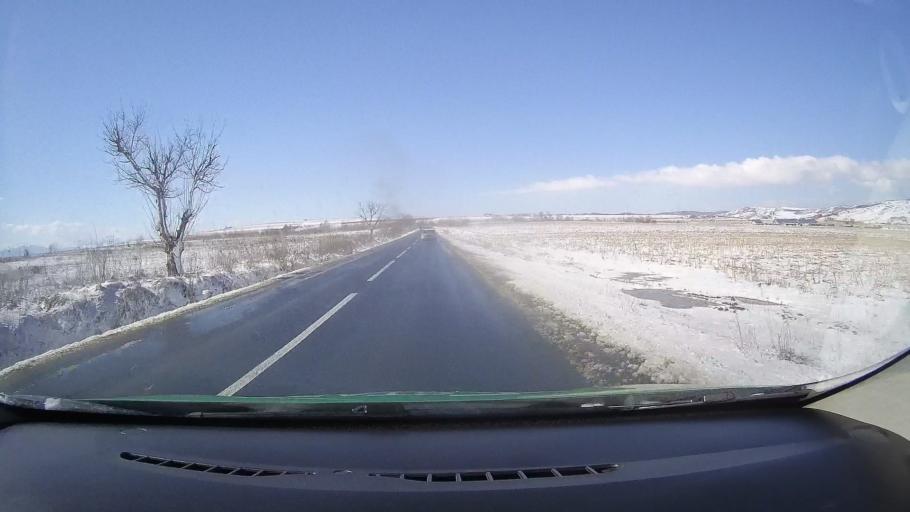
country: RO
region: Sibiu
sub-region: Comuna Rosia
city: Rosia
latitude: 45.7916
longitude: 24.3015
